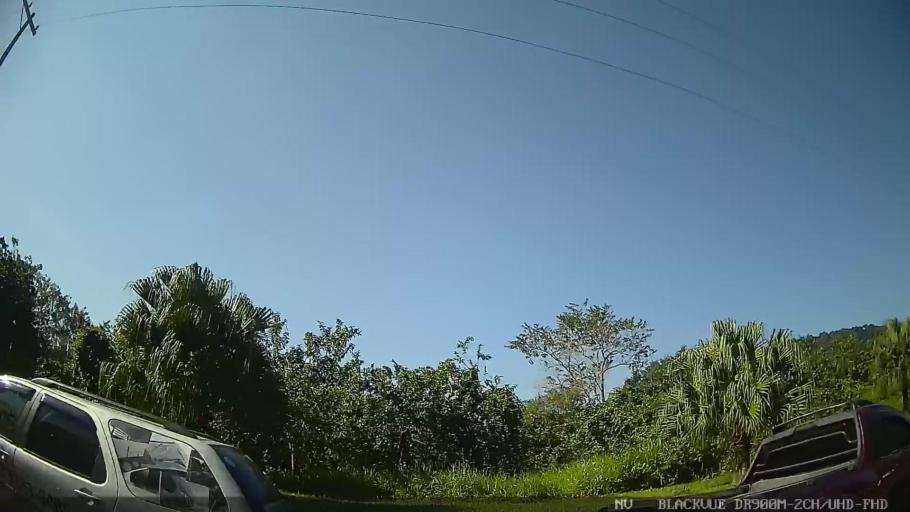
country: BR
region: Sao Paulo
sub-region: Guaruja
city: Guaruja
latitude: -24.0037
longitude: -46.2885
